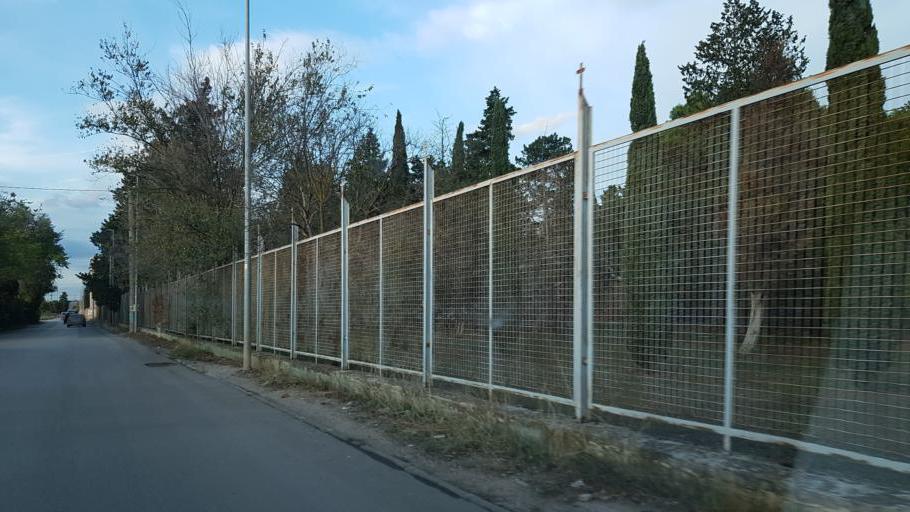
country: IT
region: Apulia
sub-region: Provincia di Foggia
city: Foggia
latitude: 41.4716
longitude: 15.5480
